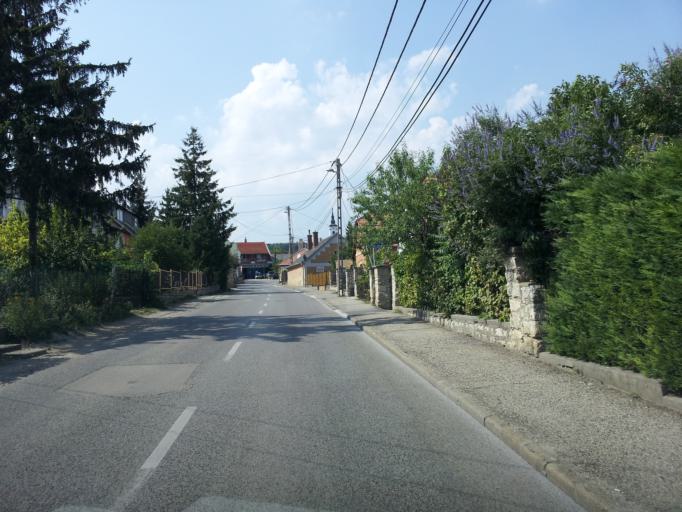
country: HU
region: Veszprem
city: Balatonfured
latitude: 46.9574
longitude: 17.8705
